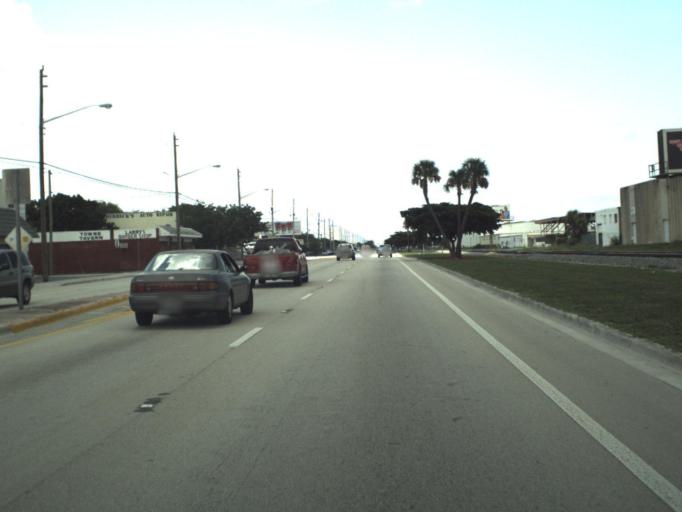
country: US
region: Florida
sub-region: Broward County
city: Kendall Green
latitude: 26.2625
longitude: -80.1173
